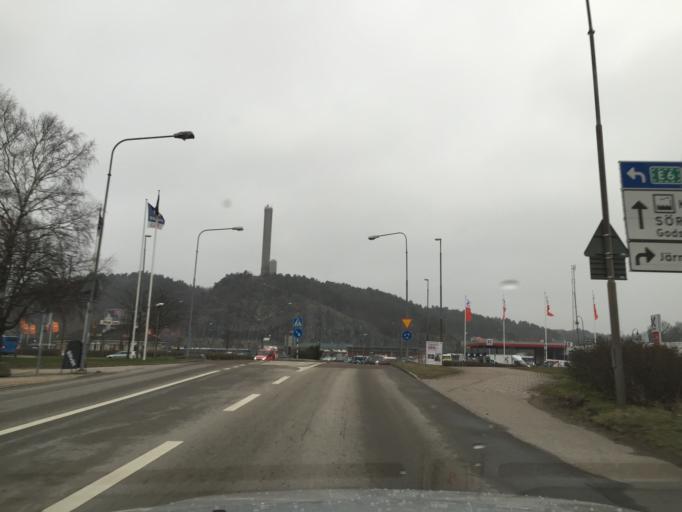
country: SE
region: Vaestra Goetaland
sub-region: Uddevalla Kommun
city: Uddevalla
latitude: 58.3522
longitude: 11.9160
